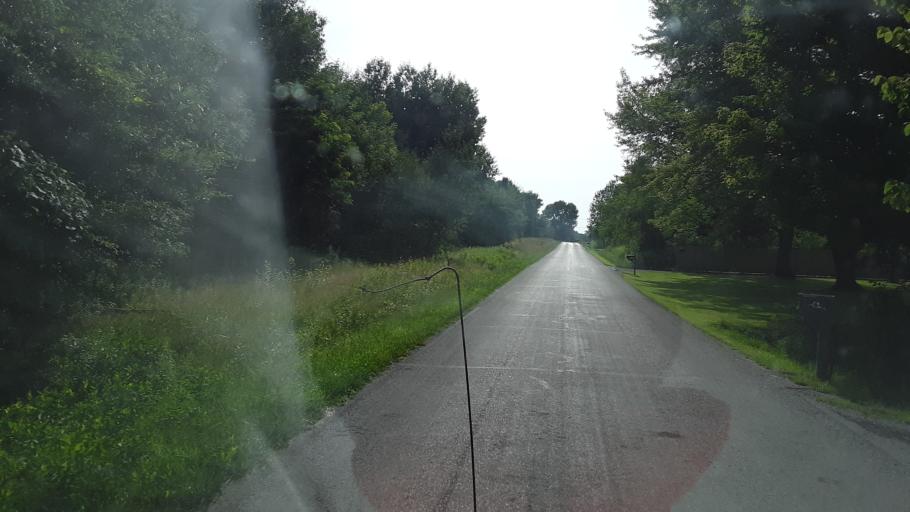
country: US
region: Ohio
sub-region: Ashtabula County
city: Jefferson
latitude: 41.6914
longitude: -80.6909
